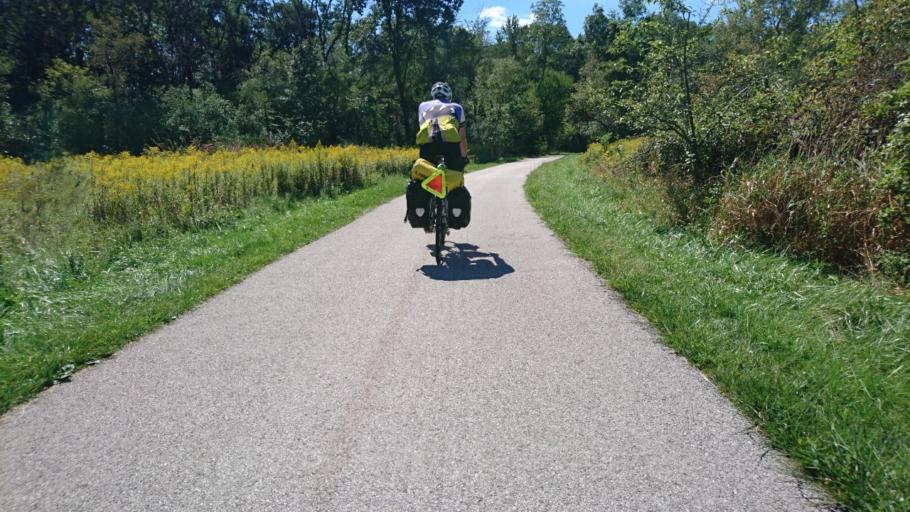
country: US
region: Illinois
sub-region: Cook County
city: Lansing
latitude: 41.5544
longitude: -87.5542
